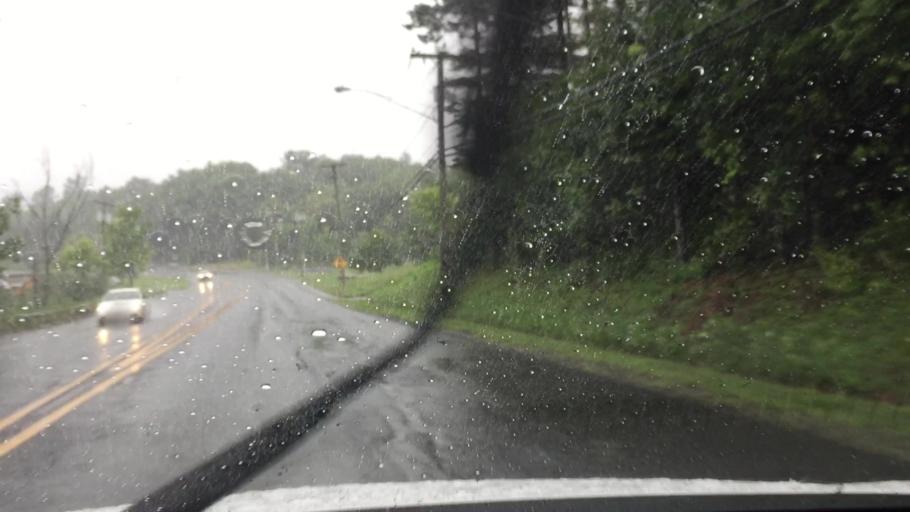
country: US
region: Massachusetts
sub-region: Berkshire County
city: Dalton
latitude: 42.4853
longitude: -73.2021
